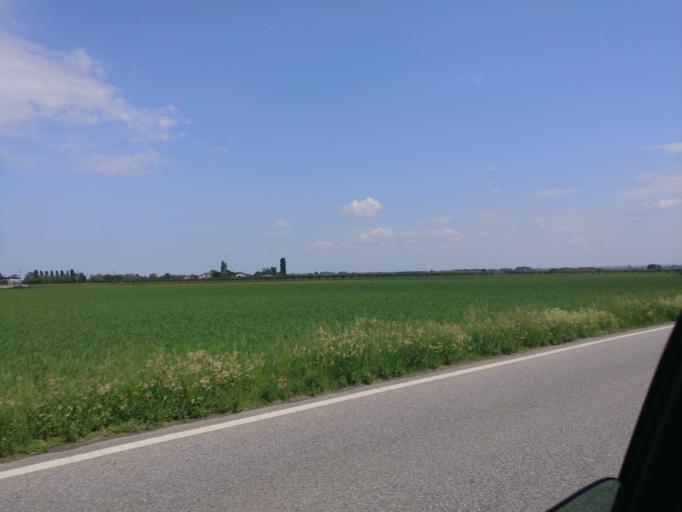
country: IT
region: Piedmont
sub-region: Provincia di Torino
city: Cavour
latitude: 44.7761
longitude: 7.3871
